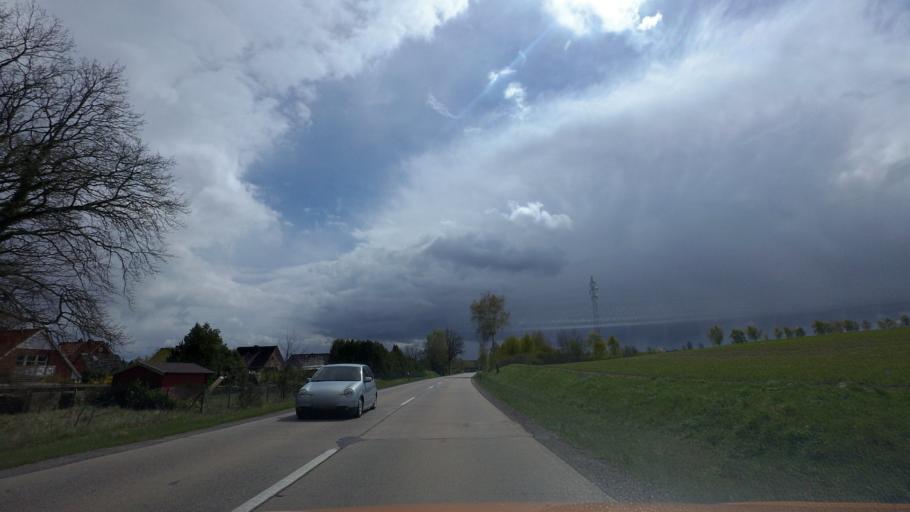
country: DE
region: Lower Saxony
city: Embsen
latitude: 53.1908
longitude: 10.3269
